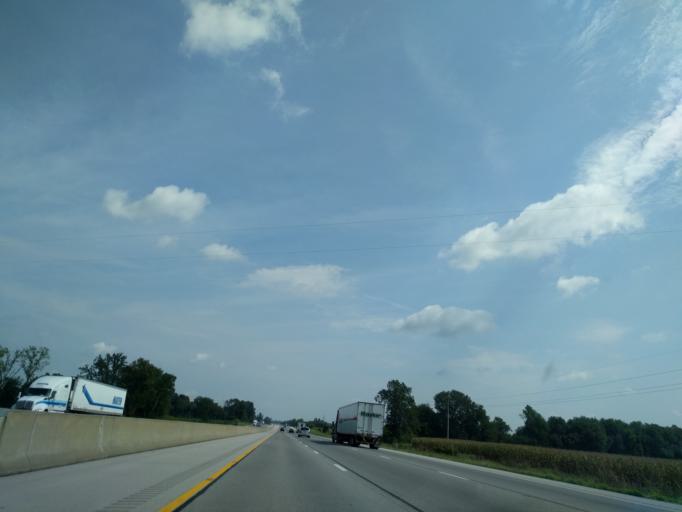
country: US
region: Kentucky
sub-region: Warren County
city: Plano
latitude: 36.8638
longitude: -86.4523
